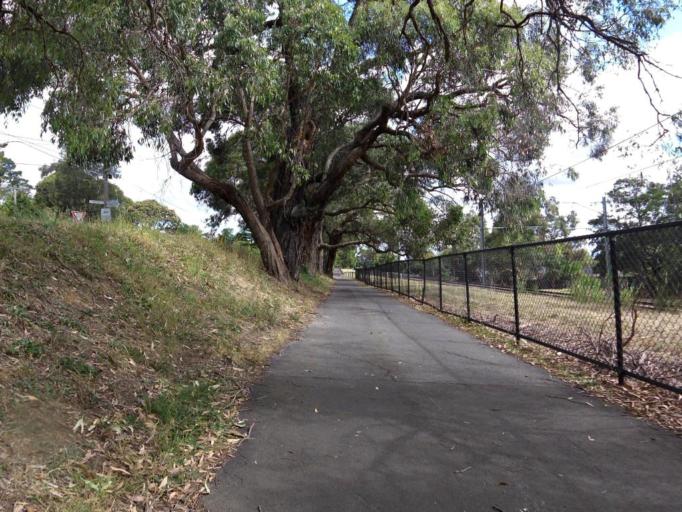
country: AU
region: Victoria
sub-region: Knox
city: Boronia
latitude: -37.8658
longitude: 145.2868
